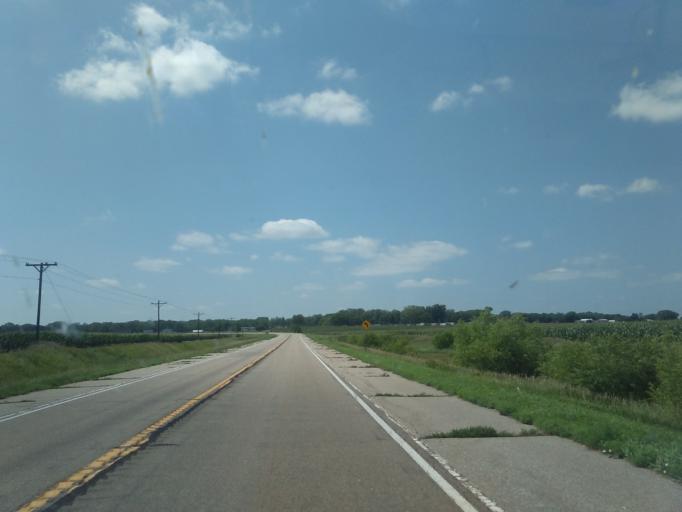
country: US
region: Nebraska
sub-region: Gosper County
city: Elwood
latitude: 40.6846
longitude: -99.8172
